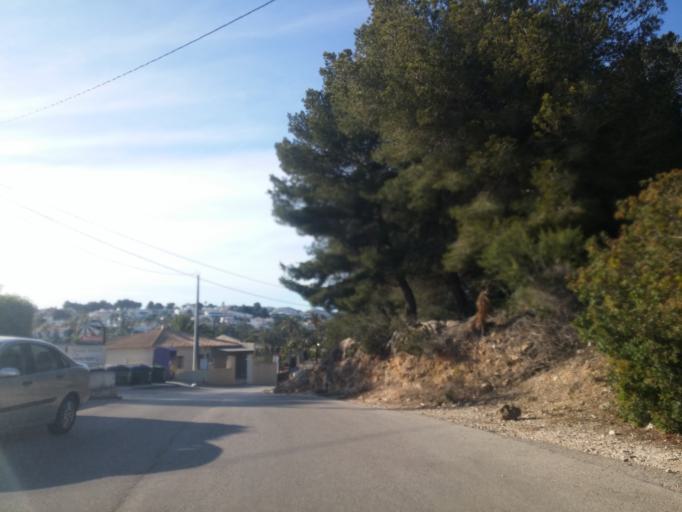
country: ES
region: Valencia
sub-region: Provincia de Alicante
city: Moraira
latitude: 38.7018
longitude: 0.1363
